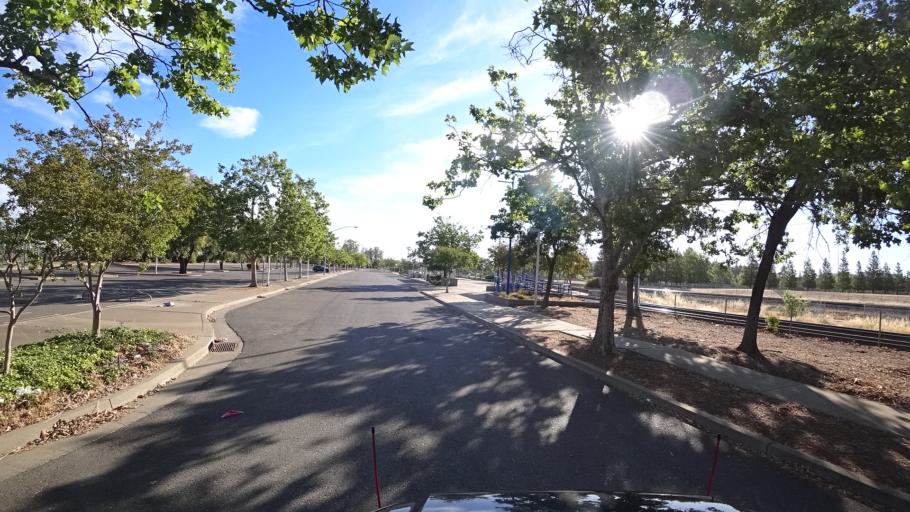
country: US
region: California
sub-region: Sacramento County
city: Sacramento
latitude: 38.6073
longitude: -121.4402
